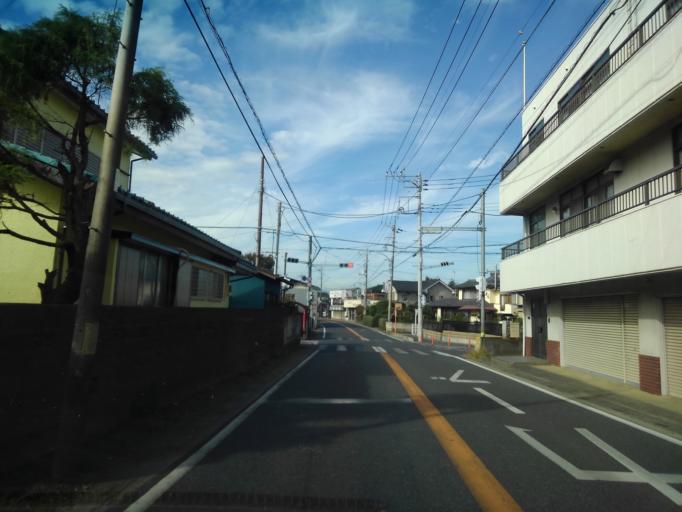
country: JP
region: Saitama
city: Sayama
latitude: 35.7935
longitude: 139.3844
